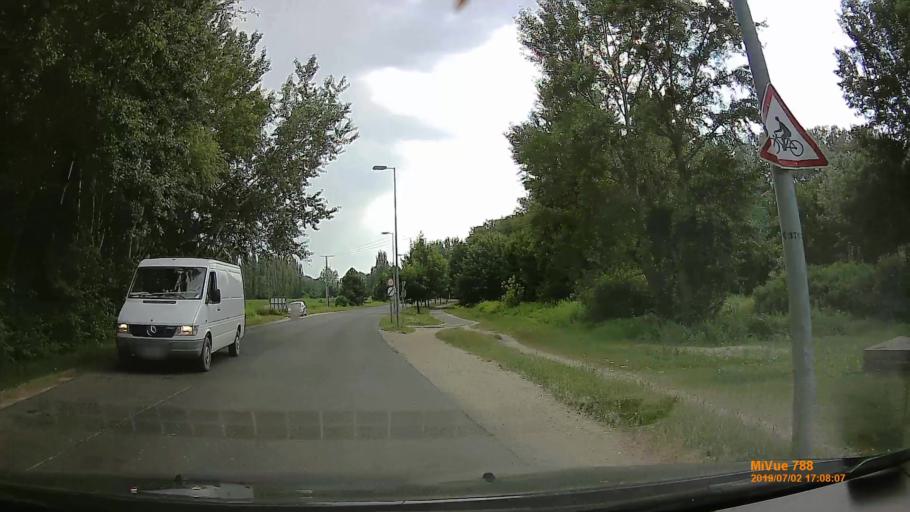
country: HU
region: Gyor-Moson-Sopron
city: Mosonmagyarovar
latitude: 47.8712
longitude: 17.2874
